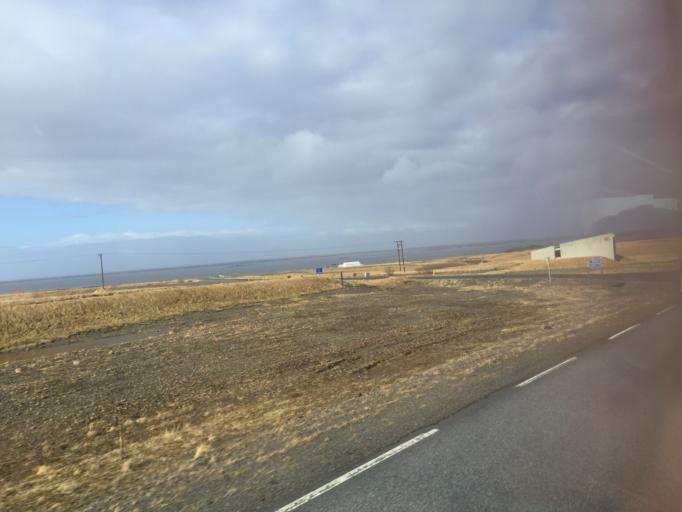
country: IS
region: West
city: Borgarnes
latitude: 64.4643
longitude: -21.9632
